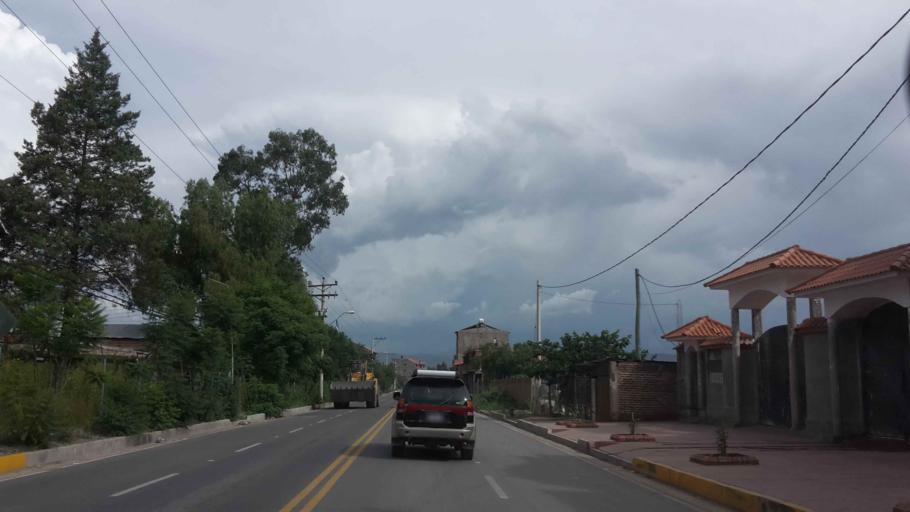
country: BO
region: Cochabamba
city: Cochabamba
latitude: -17.3502
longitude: -66.2567
